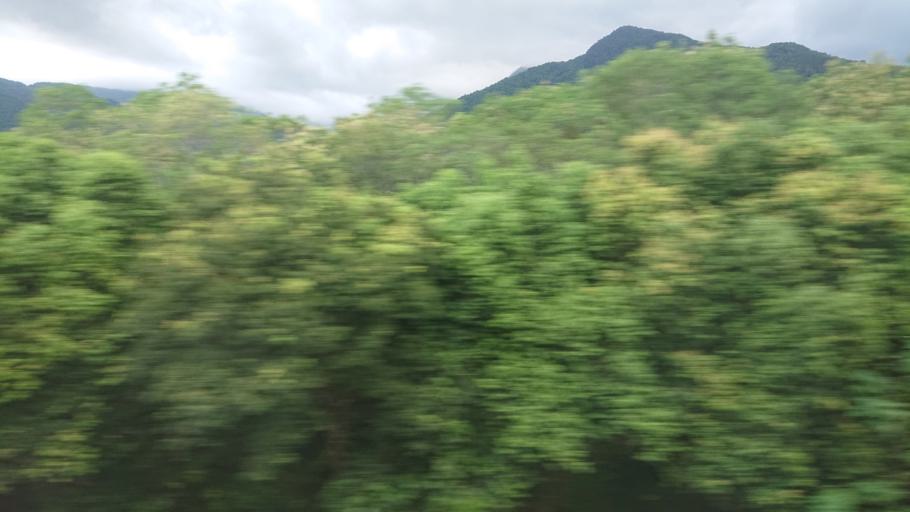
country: TW
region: Taiwan
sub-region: Hualien
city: Hualian
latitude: 23.6122
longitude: 121.3915
